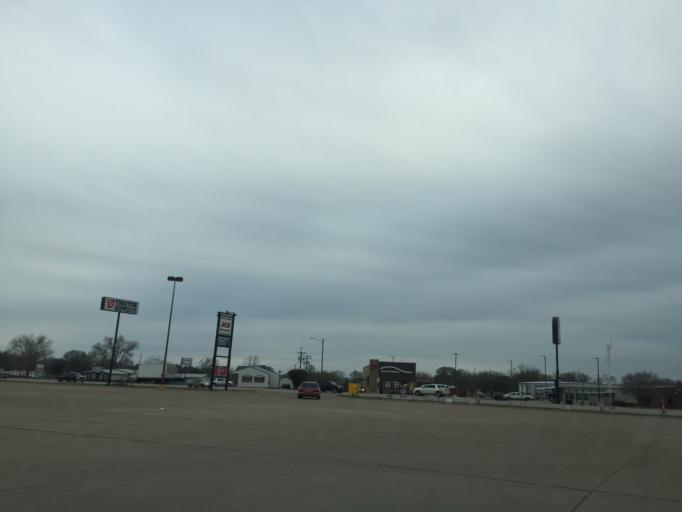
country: US
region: Texas
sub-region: Coryell County
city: Gatesville
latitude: 31.4343
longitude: -97.7306
